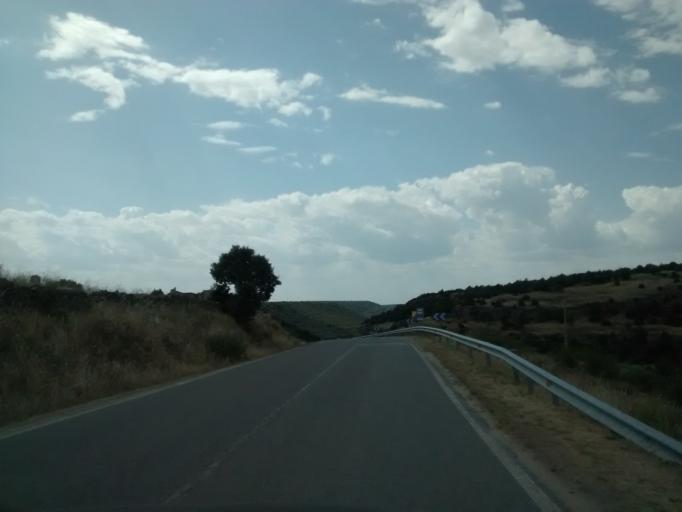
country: ES
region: Castille and Leon
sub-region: Provincia de Segovia
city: Pedraza
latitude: 41.1305
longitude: -3.8043
